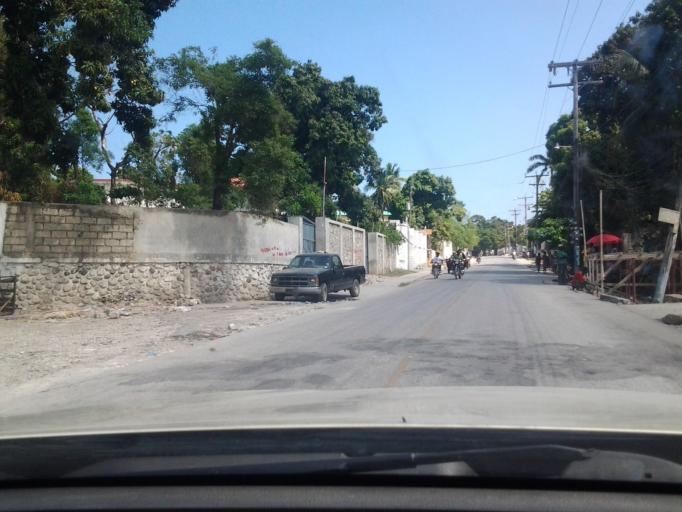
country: HT
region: Ouest
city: Tigwav
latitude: 18.4346
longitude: -72.8621
